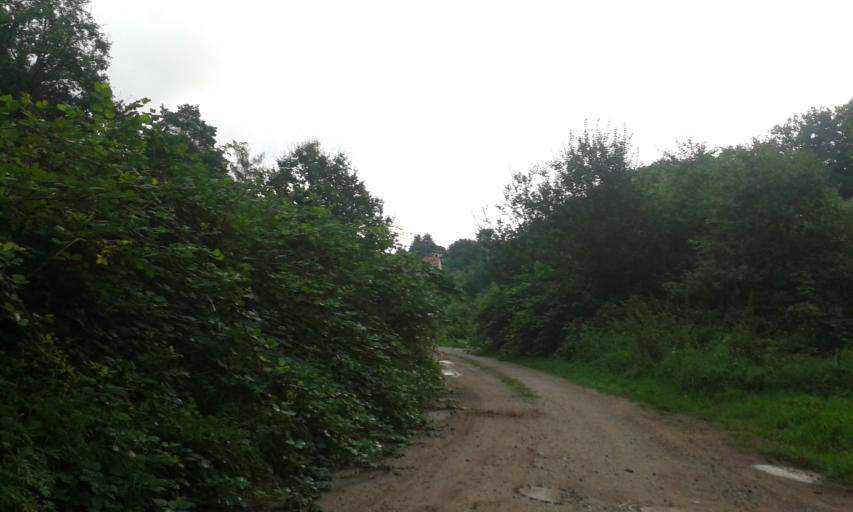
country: DE
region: Bavaria
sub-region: Upper Franconia
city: Bamberg
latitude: 49.8723
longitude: 10.8990
